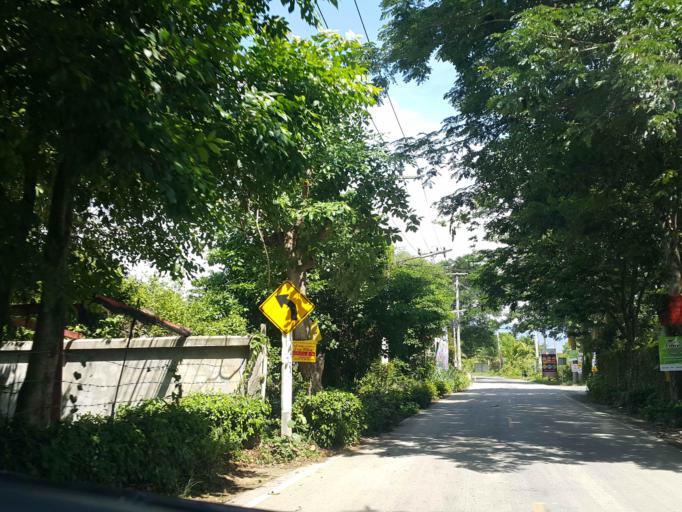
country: TH
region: Chiang Mai
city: Saraphi
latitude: 18.7476
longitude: 99.0667
